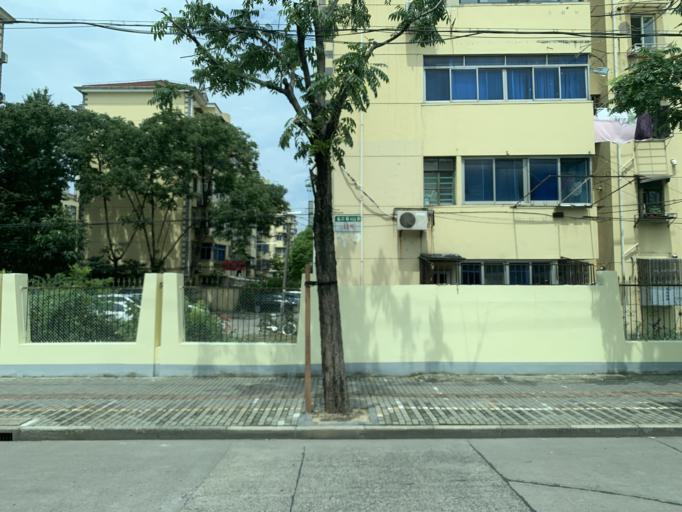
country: CN
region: Shanghai Shi
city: Huamu
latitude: 31.2490
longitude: 121.5756
